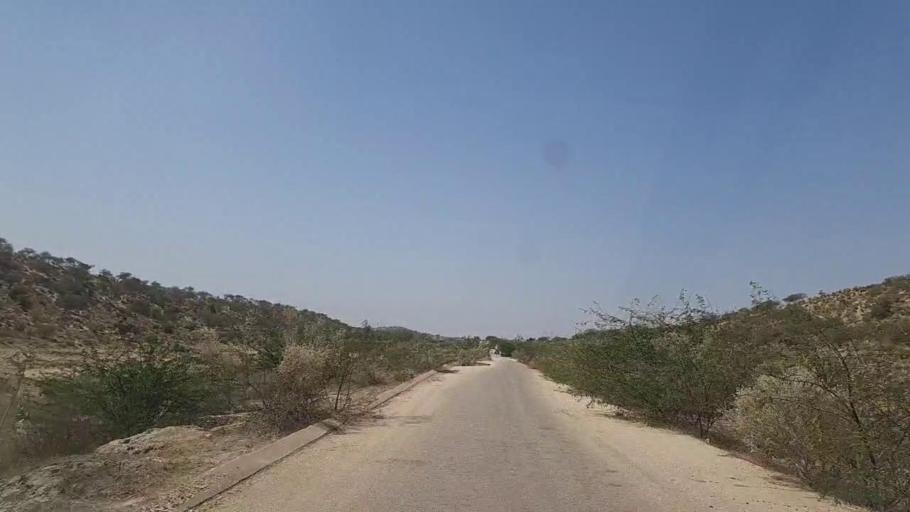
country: PK
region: Sindh
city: Diplo
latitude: 24.5156
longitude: 69.3398
